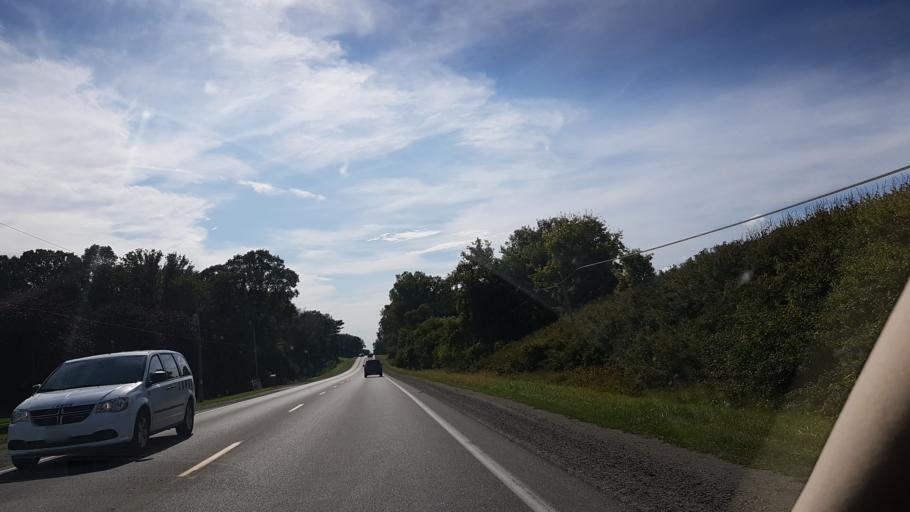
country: CA
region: Ontario
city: Delaware
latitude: 42.9393
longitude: -81.4390
